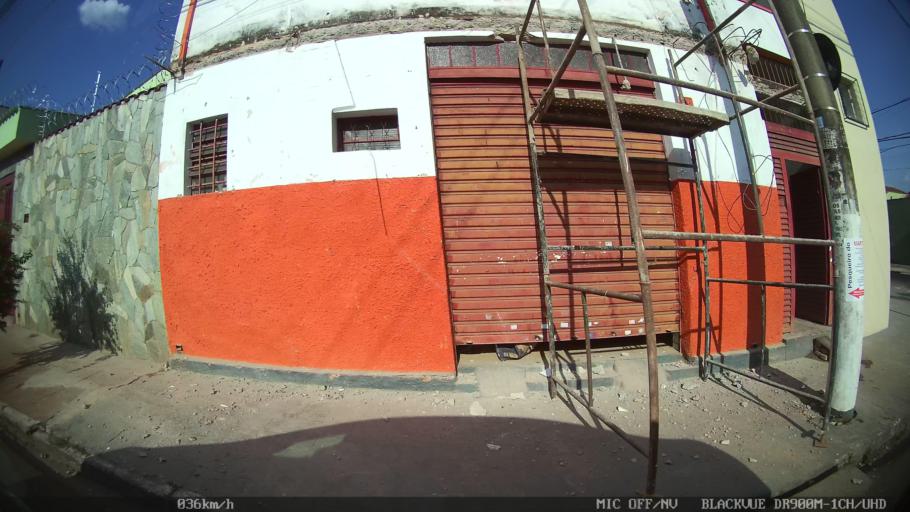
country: BR
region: Sao Paulo
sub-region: Ribeirao Preto
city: Ribeirao Preto
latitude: -21.1598
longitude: -47.8082
